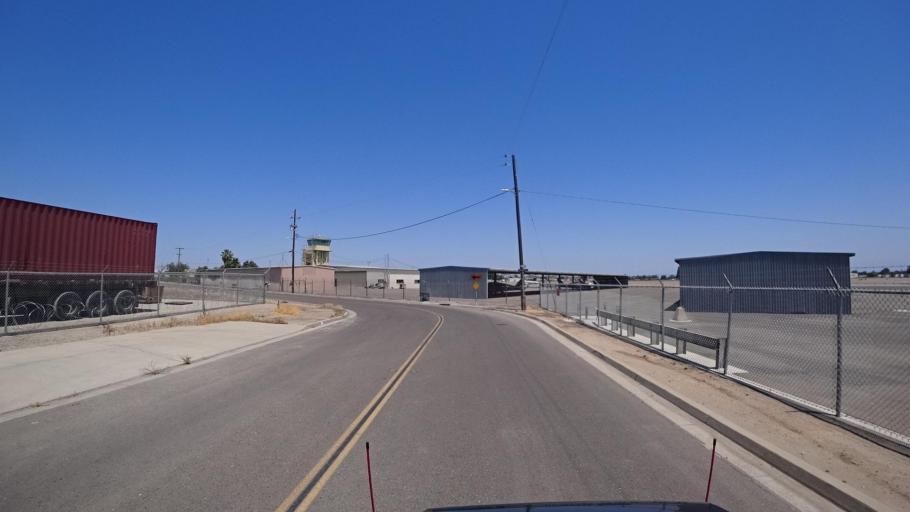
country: US
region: California
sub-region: Fresno County
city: West Park
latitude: 36.7303
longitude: -119.8221
